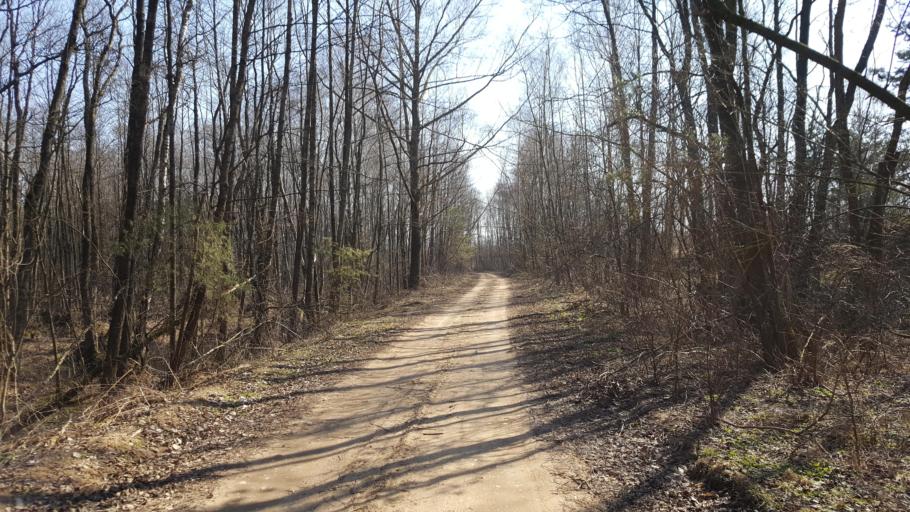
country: BY
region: Brest
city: Kamyanyets
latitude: 52.3677
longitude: 23.7513
